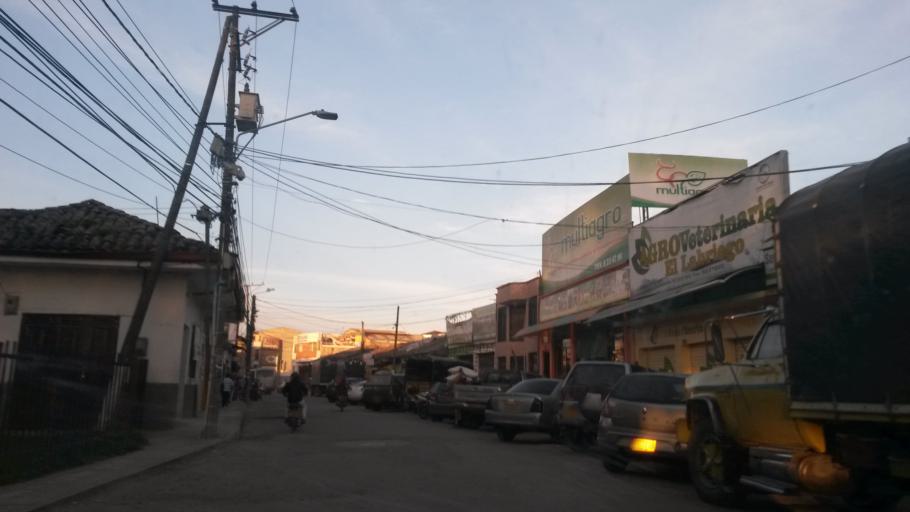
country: CO
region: Cauca
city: Popayan
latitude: 2.4485
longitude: -76.6021
